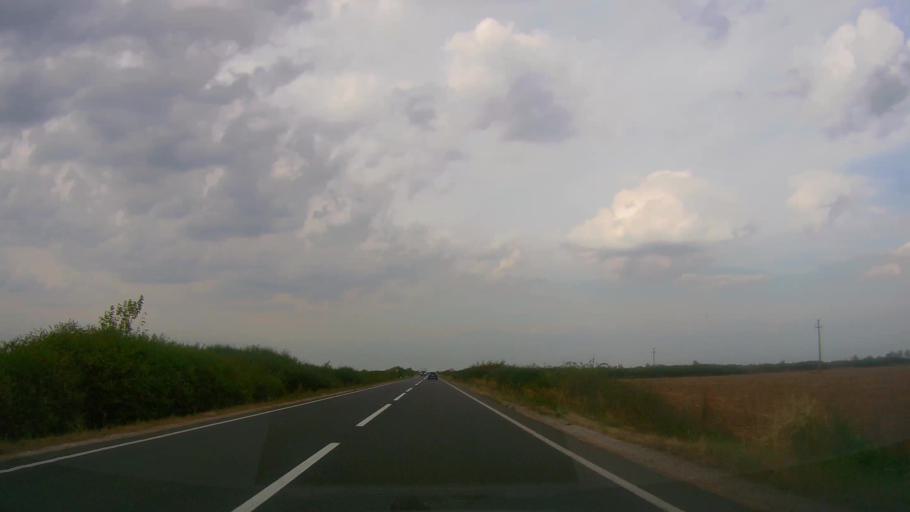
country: RO
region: Satu Mare
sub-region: Comuna Acas
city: Acas
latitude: 47.5393
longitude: 22.8105
